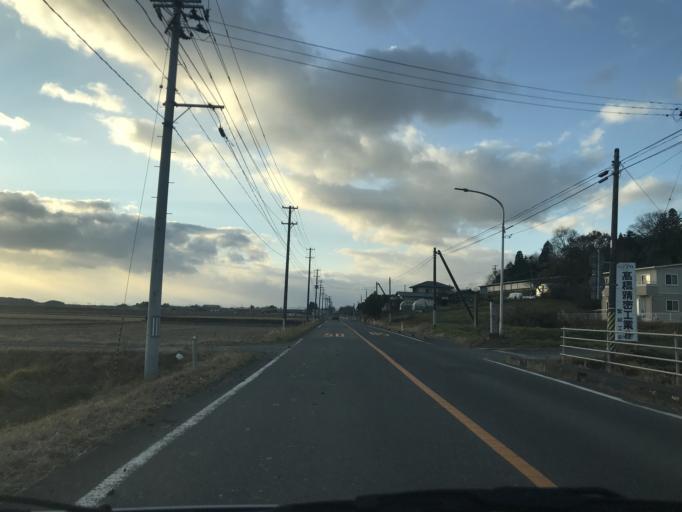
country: JP
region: Miyagi
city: Kogota
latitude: 38.6559
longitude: 141.0370
